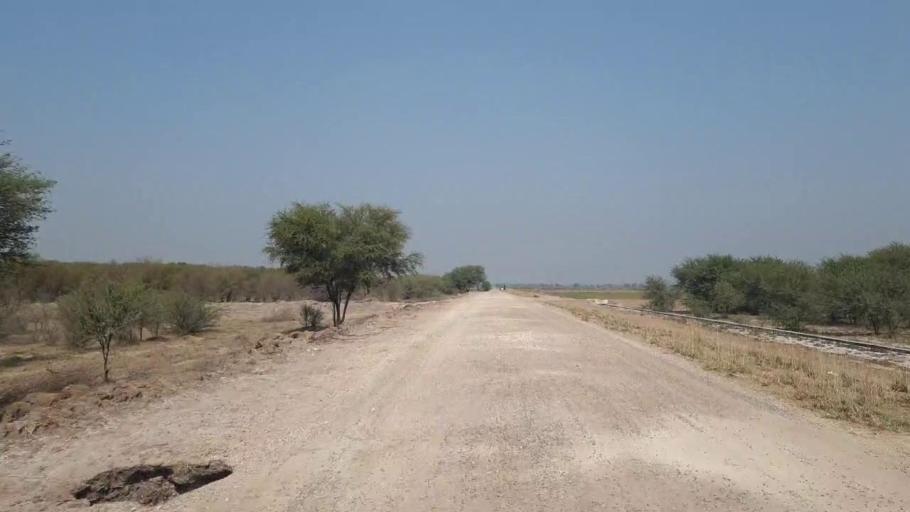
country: PK
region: Sindh
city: Mirwah Gorchani
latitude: 25.3599
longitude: 68.9316
